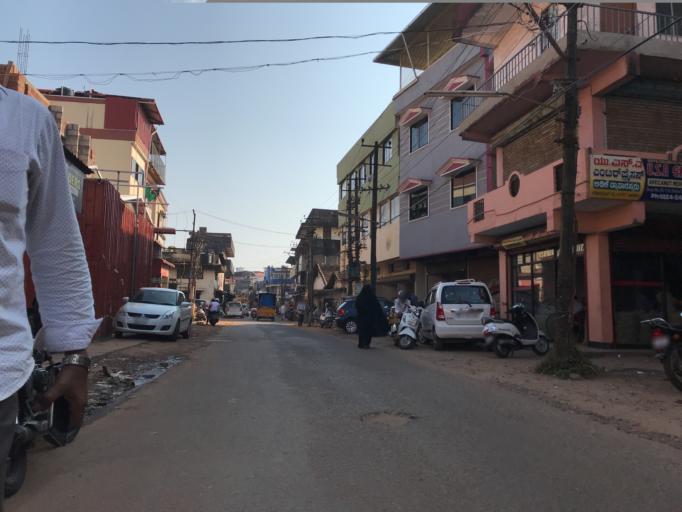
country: IN
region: Karnataka
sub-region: Dakshina Kannada
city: Mangalore
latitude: 12.8629
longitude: 74.8337
